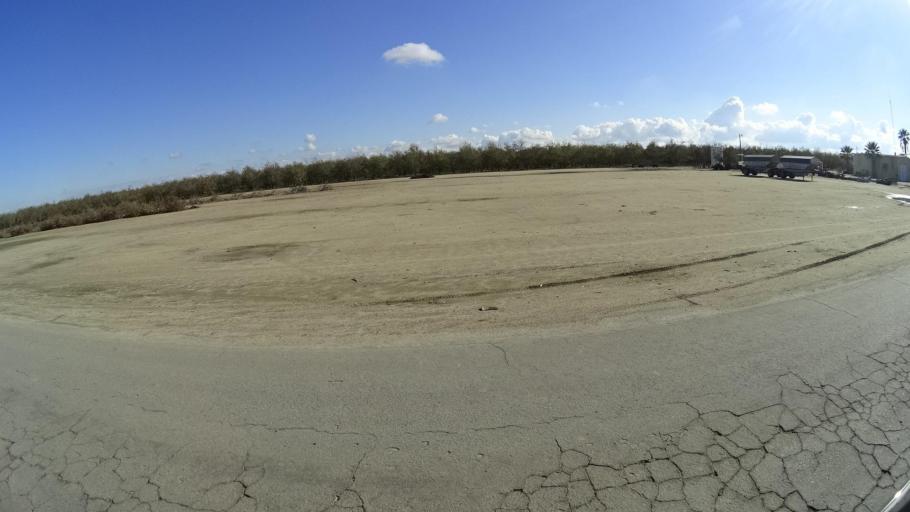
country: US
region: California
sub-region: Kern County
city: McFarland
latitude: 35.6980
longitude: -119.2588
